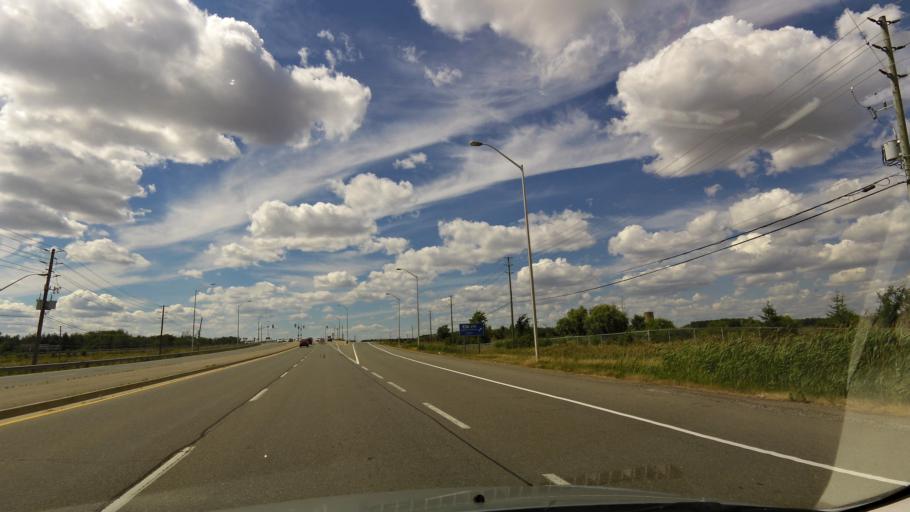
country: CA
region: Ontario
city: Burlington
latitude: 43.4428
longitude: -79.7864
